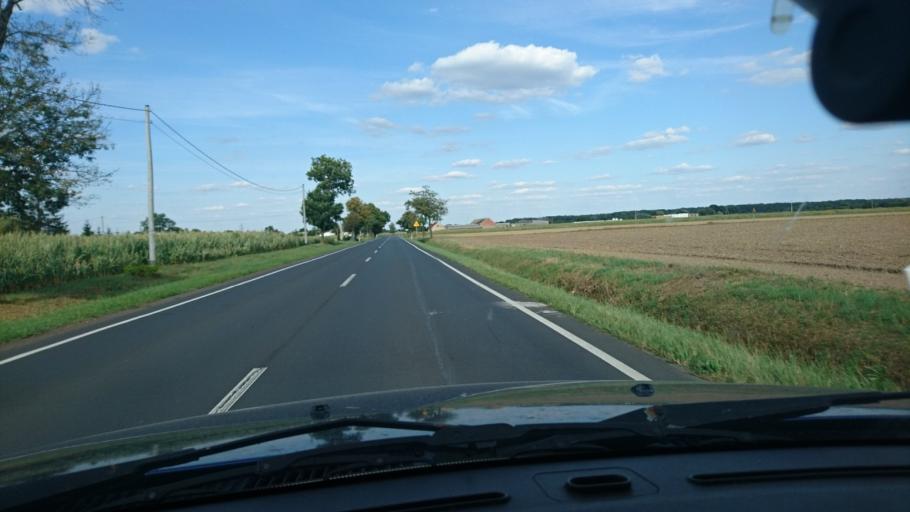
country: PL
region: Greater Poland Voivodeship
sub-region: Powiat krotoszynski
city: Kobylin
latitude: 51.7211
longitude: 17.2597
